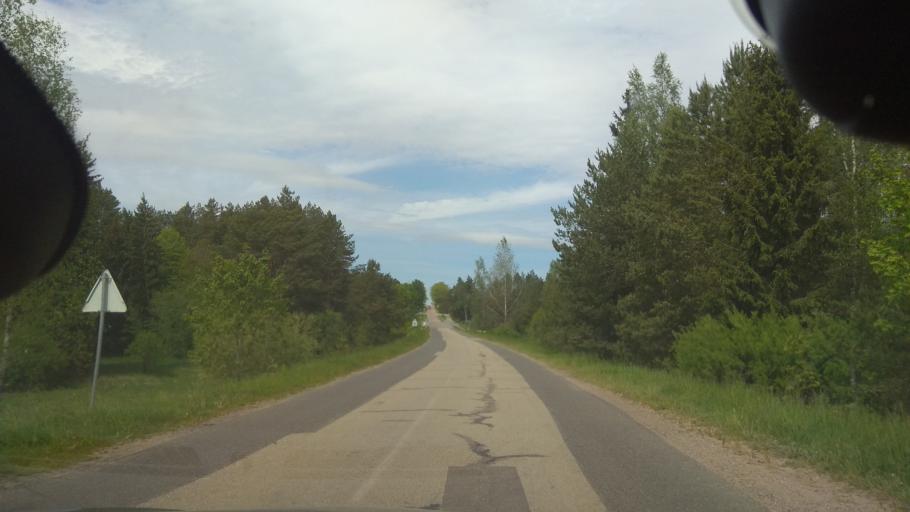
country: LT
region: Vilnius County
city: Ukmerge
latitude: 55.1377
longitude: 24.5936
